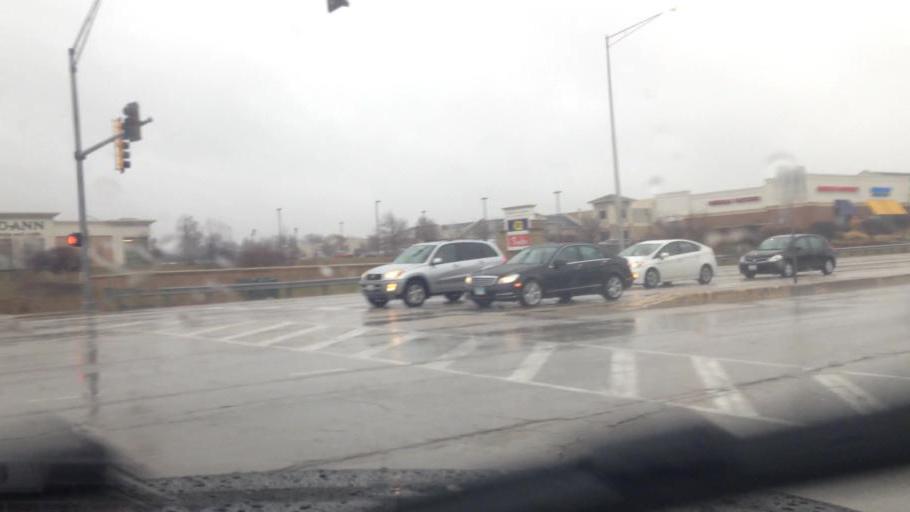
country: US
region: Illinois
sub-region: McHenry County
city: Lake in the Hills
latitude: 42.1538
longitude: -88.3359
